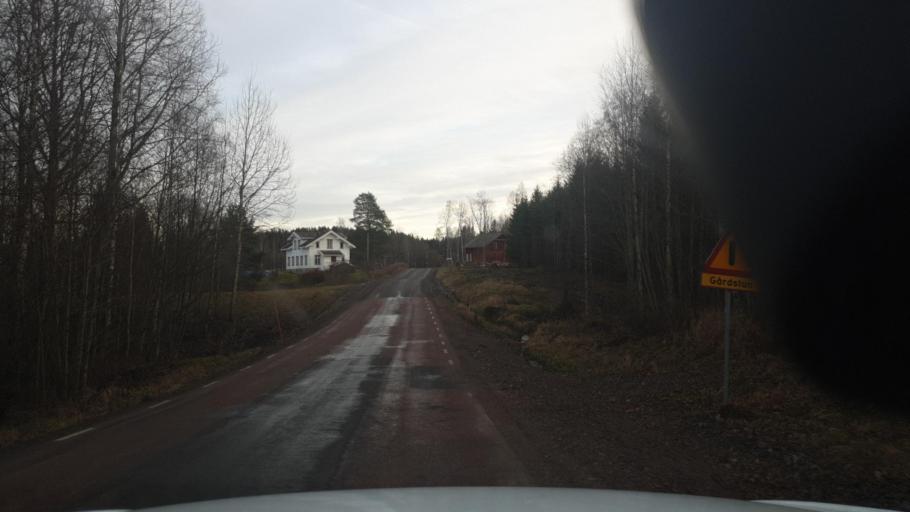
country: NO
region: Ostfold
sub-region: Romskog
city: Romskog
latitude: 59.8212
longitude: 11.9758
